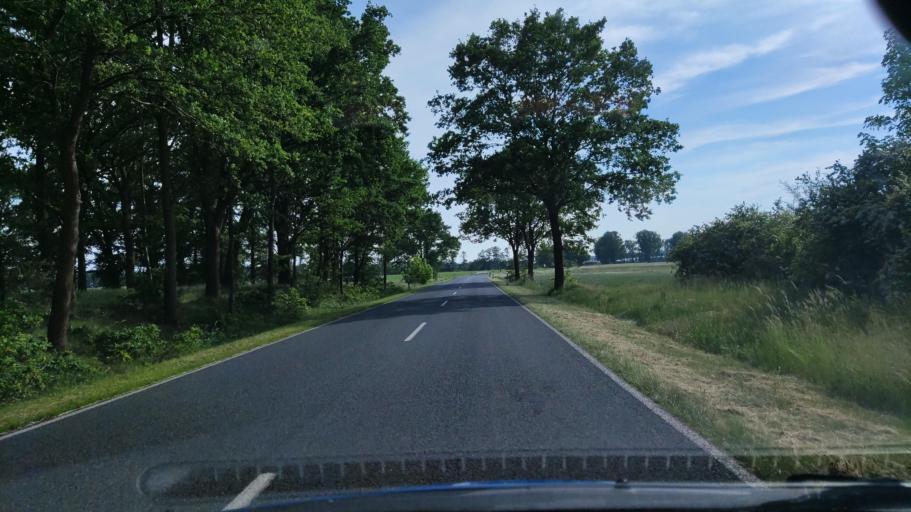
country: DE
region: Saxony-Anhalt
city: Klotze
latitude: 52.6408
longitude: 11.1837
